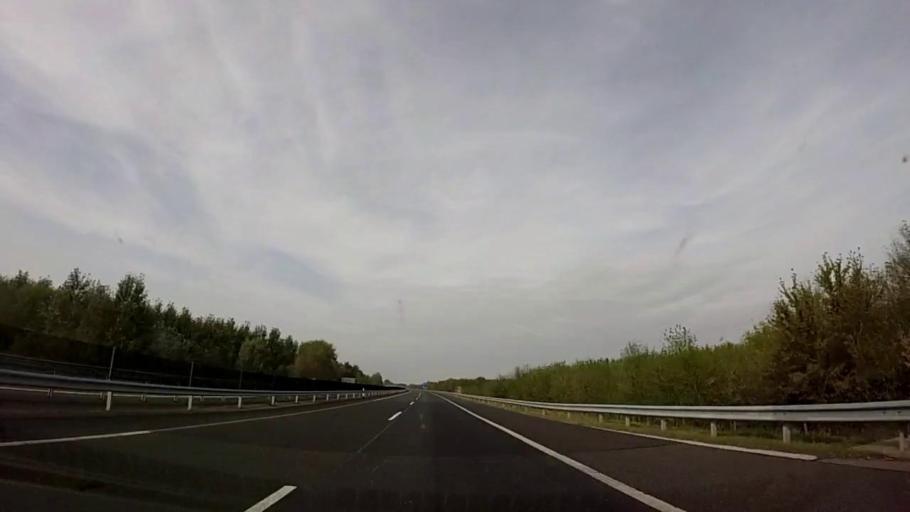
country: HU
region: Somogy
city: Balatonfenyves
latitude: 46.7027
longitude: 17.4978
